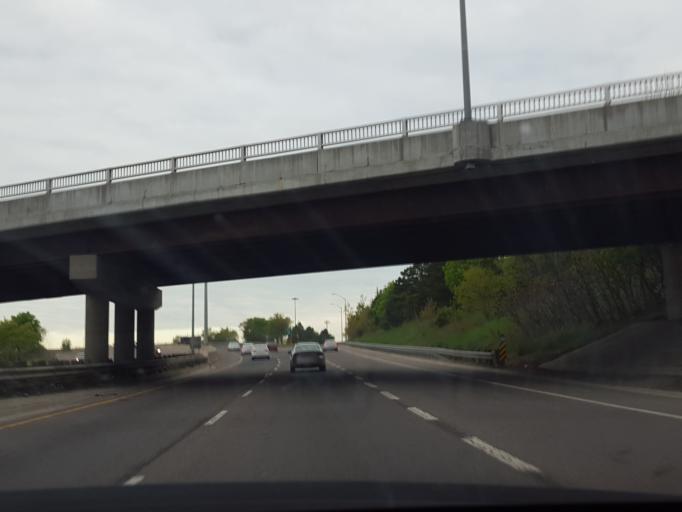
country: CA
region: Ontario
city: Toronto
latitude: 43.7097
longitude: -79.5008
